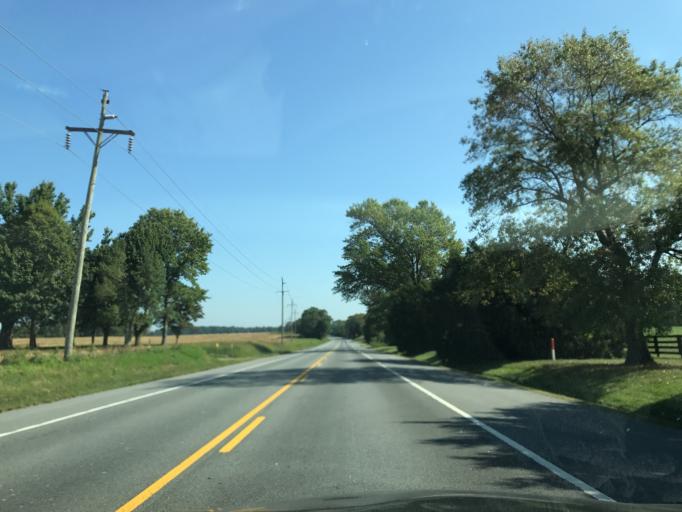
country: US
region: Maryland
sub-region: Queen Anne's County
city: Kingstown
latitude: 39.2487
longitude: -76.0136
